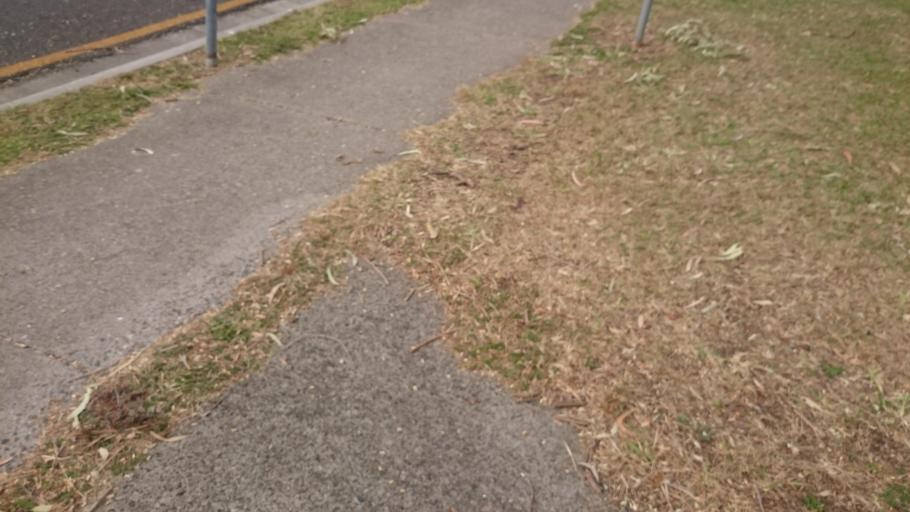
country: AU
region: Queensland
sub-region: Redland
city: Cleveland
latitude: -27.5304
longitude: 153.2667
